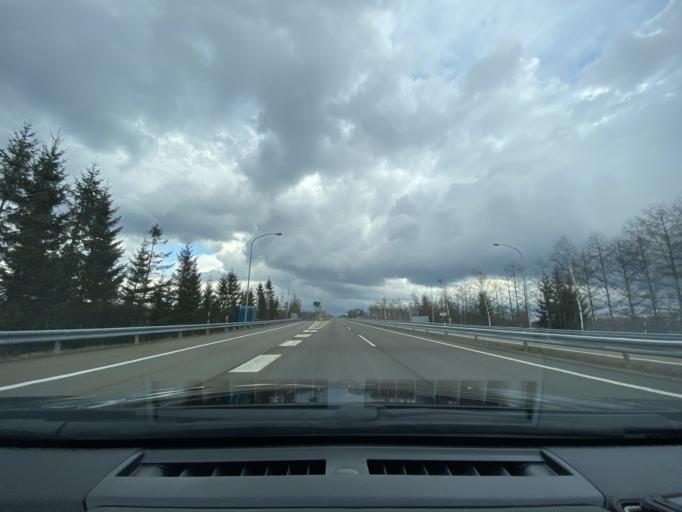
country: JP
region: Hokkaido
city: Otofuke
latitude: 42.9807
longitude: 143.1756
